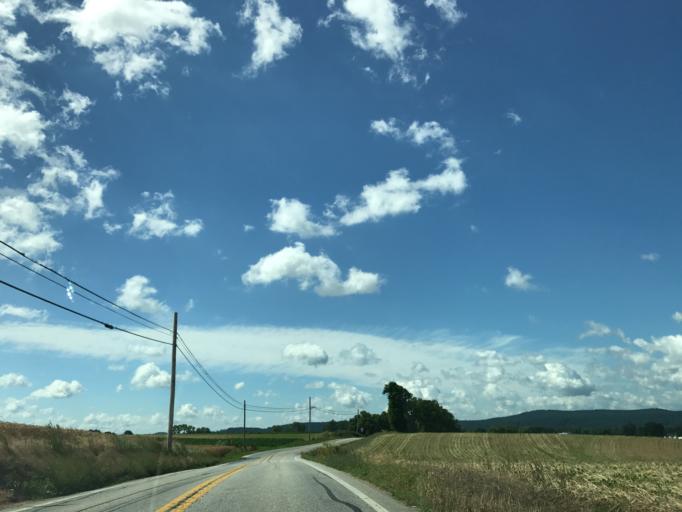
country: US
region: Pennsylvania
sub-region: Lancaster County
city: Maytown
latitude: 40.0975
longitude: -76.5909
